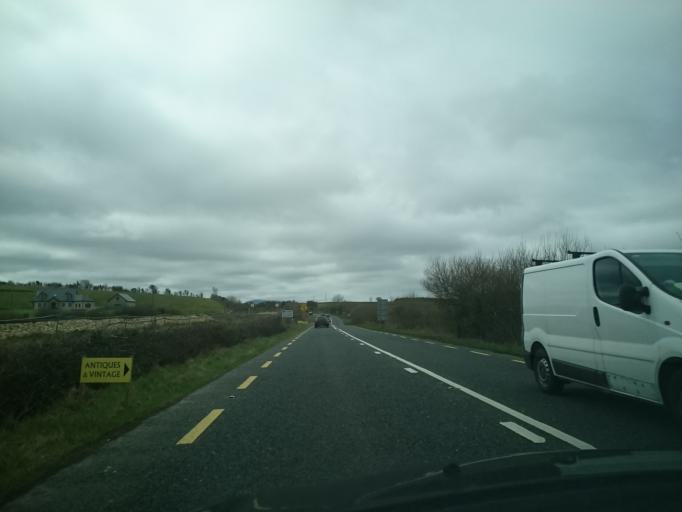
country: IE
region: Connaught
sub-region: Maigh Eo
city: Westport
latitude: 53.8124
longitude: -9.4144
